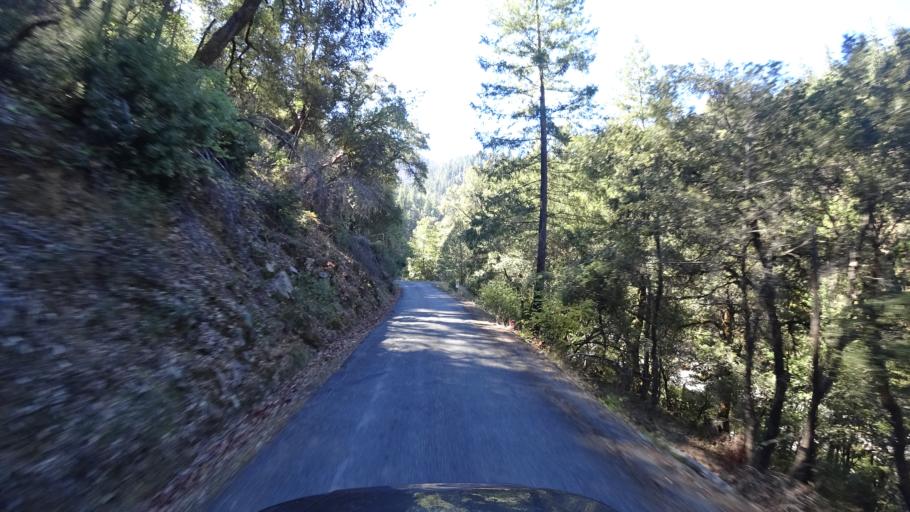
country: US
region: California
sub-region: Siskiyou County
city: Happy Camp
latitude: 41.3386
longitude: -123.3898
